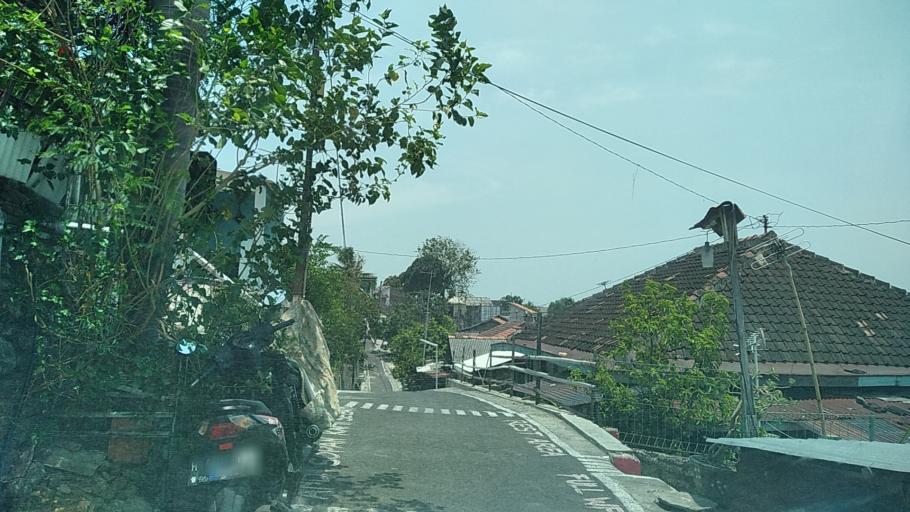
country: ID
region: Central Java
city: Semarang
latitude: -7.0122
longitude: 110.4507
